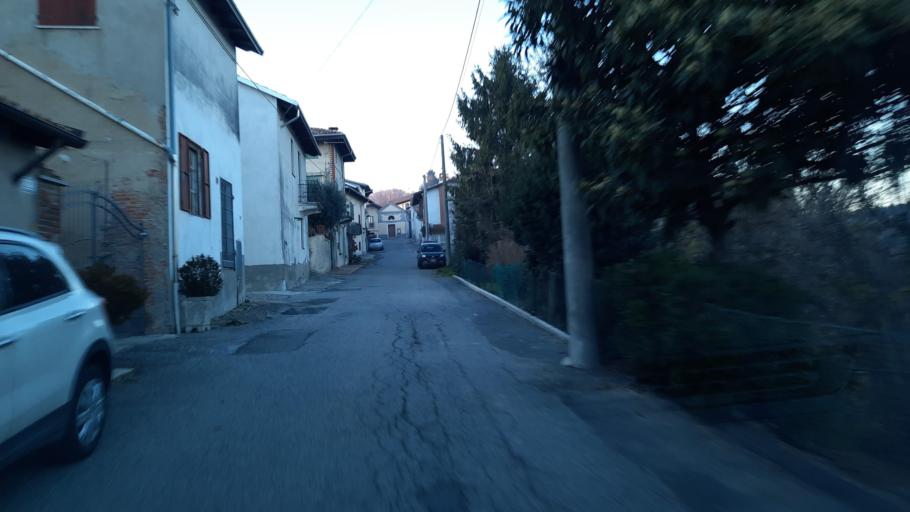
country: IT
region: Piedmont
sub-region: Provincia di Alessandria
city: Camino
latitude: 45.1574
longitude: 8.2837
